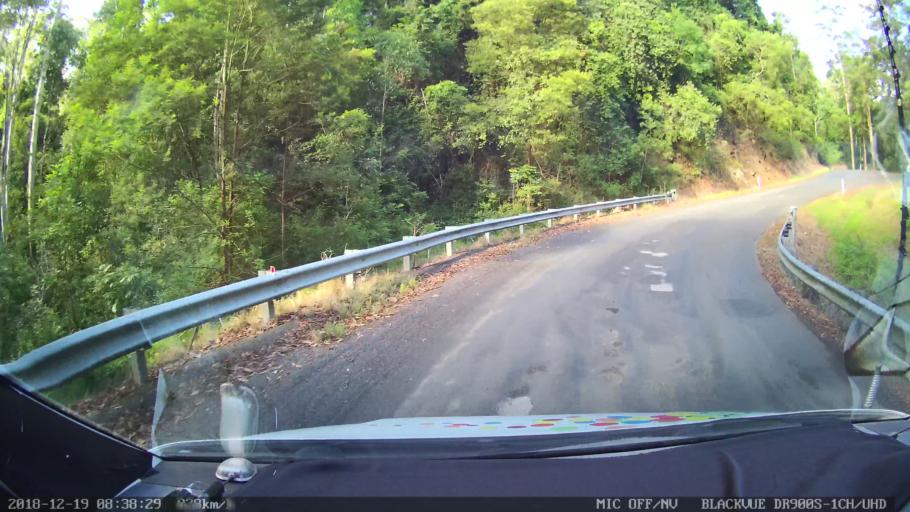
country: AU
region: New South Wales
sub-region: Kyogle
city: Kyogle
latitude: -28.3353
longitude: 152.9750
